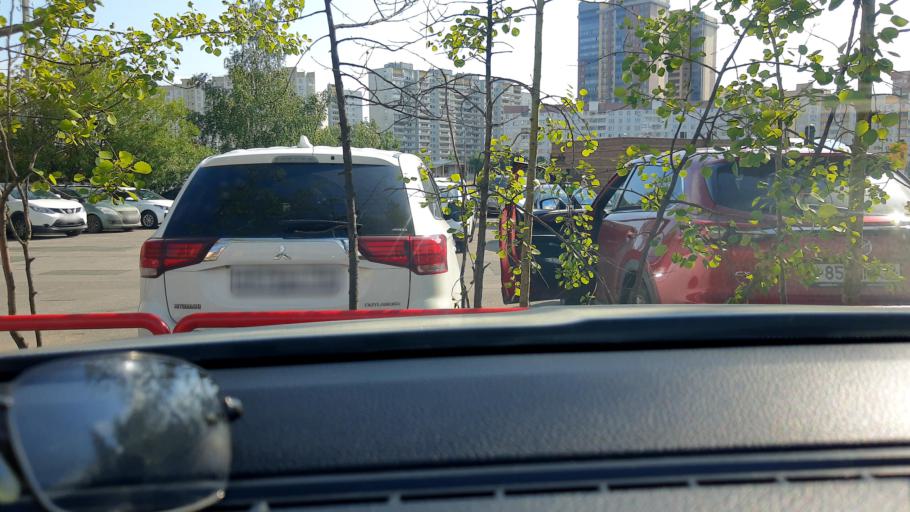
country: RU
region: Moskovskaya
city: Odintsovo
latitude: 55.6904
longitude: 37.3054
